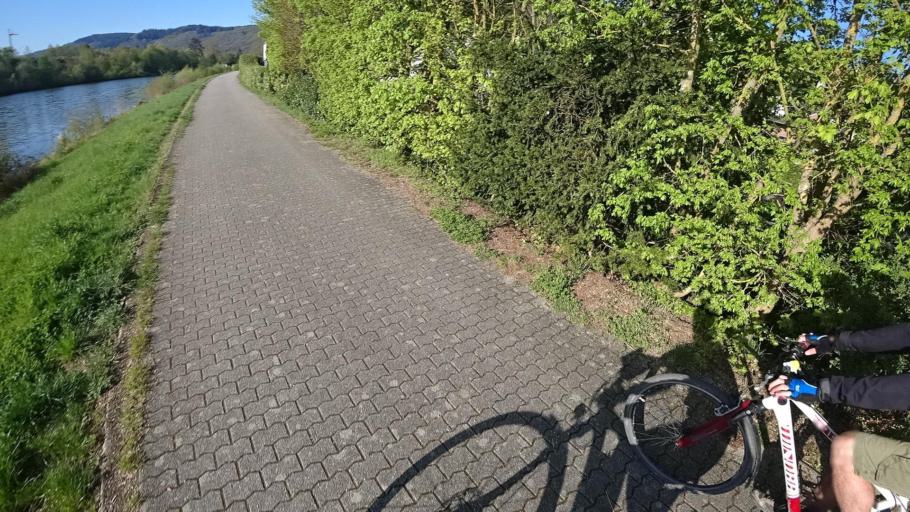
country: DE
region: Rheinland-Pfalz
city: Saarburg
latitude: 49.6128
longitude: 6.5610
